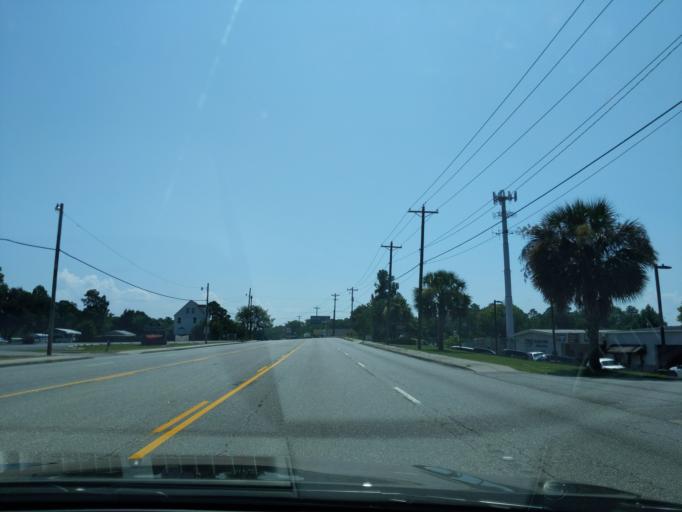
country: US
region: South Carolina
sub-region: Lexington County
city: Oak Grove
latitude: 33.9721
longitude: -81.1475
